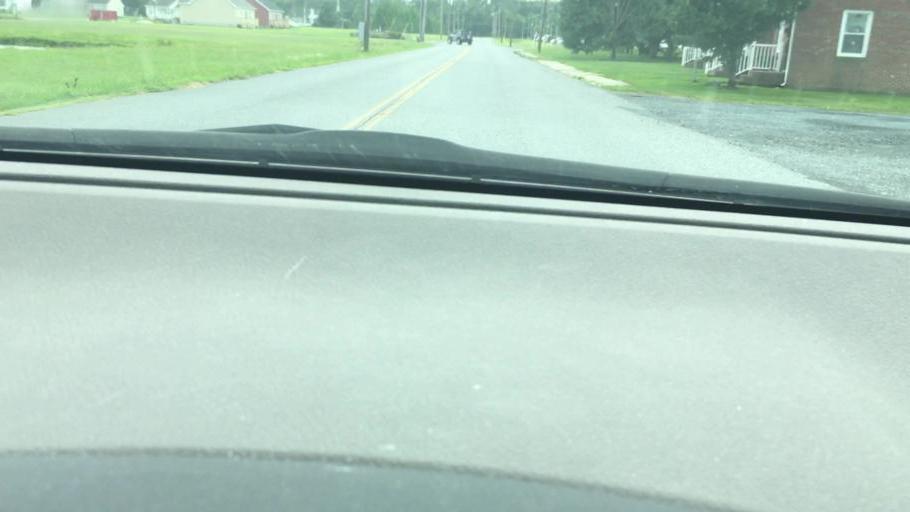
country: US
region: Maryland
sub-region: Worcester County
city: Pocomoke City
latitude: 38.0614
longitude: -75.5501
